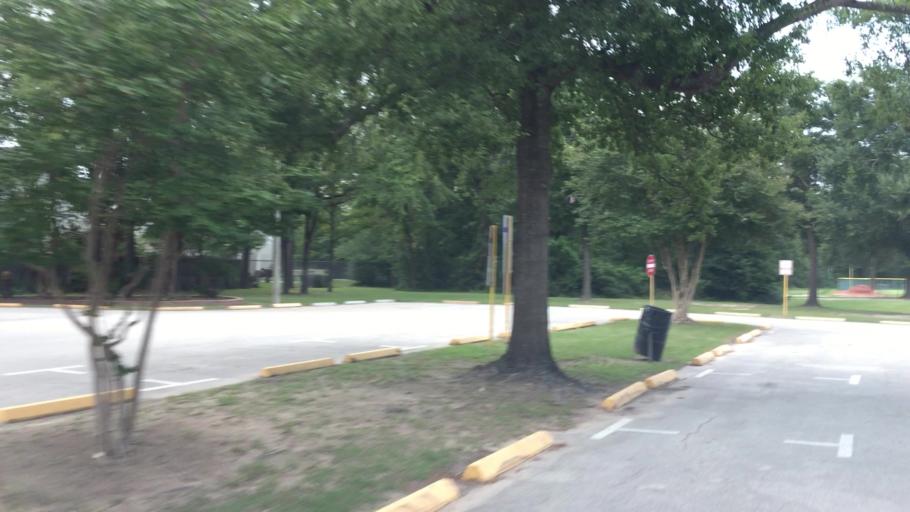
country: US
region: Texas
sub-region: Harris County
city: Hudson
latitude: 30.0129
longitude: -95.5083
